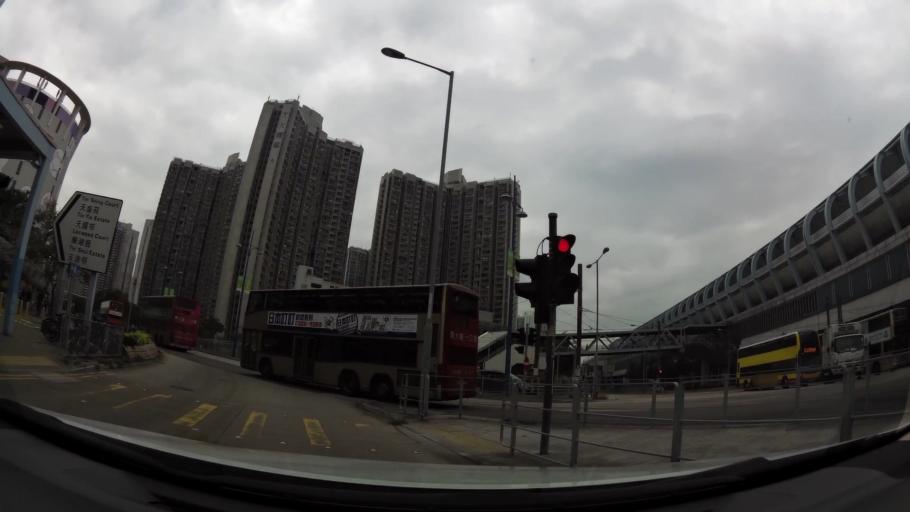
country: HK
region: Yuen Long
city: Yuen Long Kau Hui
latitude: 22.4478
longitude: 114.0037
